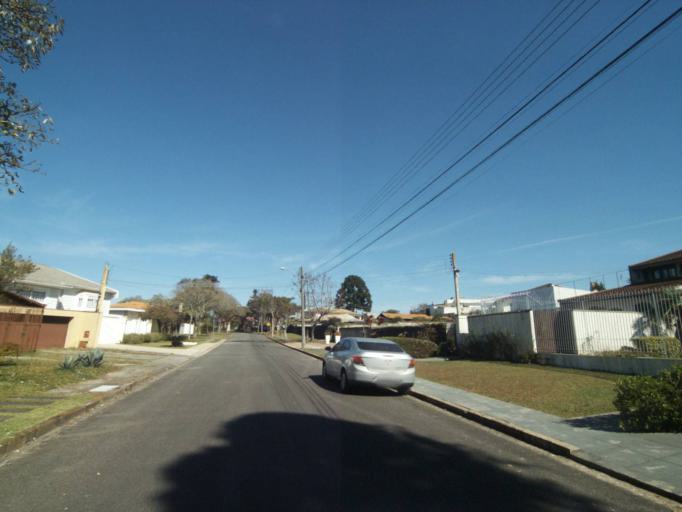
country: BR
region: Parana
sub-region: Curitiba
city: Curitiba
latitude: -25.4129
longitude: -49.2363
